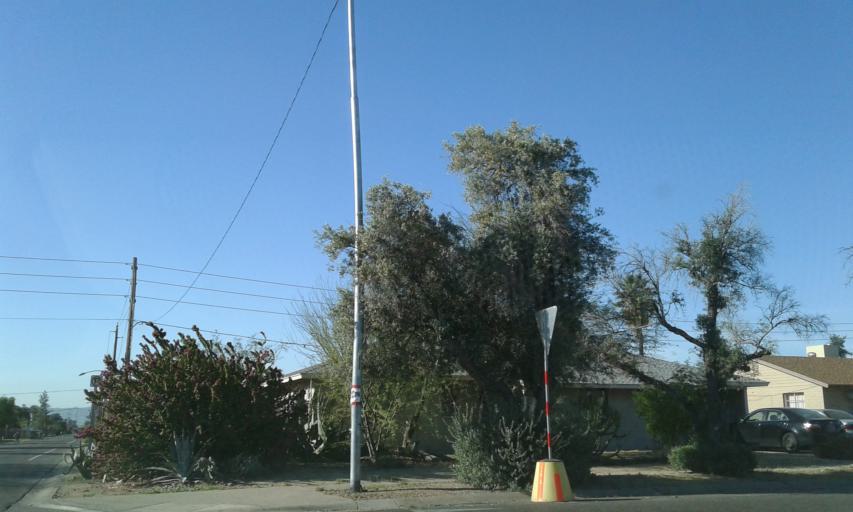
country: US
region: Arizona
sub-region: Maricopa County
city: Phoenix
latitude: 33.4879
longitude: -112.1085
